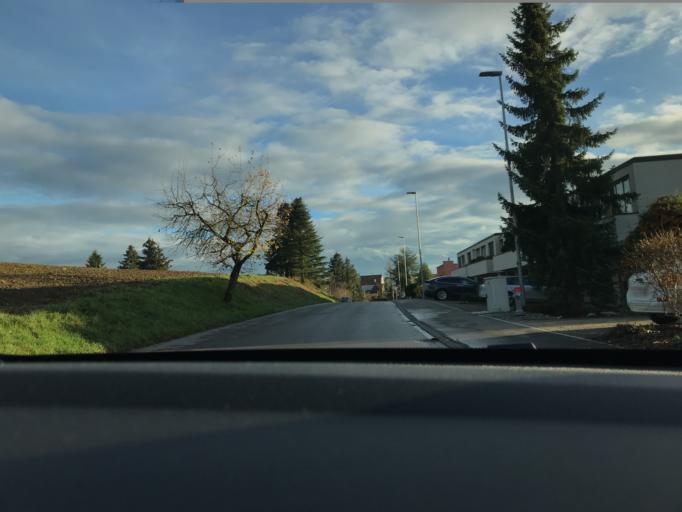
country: CH
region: Zurich
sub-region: Bezirk Dielsdorf
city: Hofstetten
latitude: 47.4709
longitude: 8.5014
